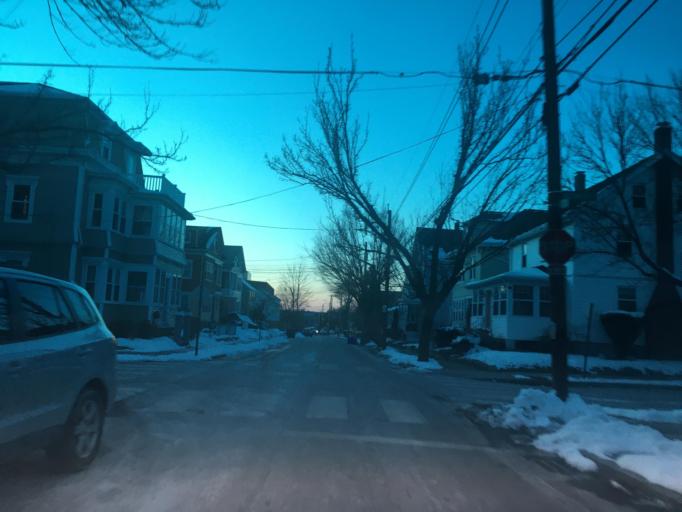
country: US
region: Rhode Island
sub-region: Providence County
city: Providence
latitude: 41.8506
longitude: -71.3965
